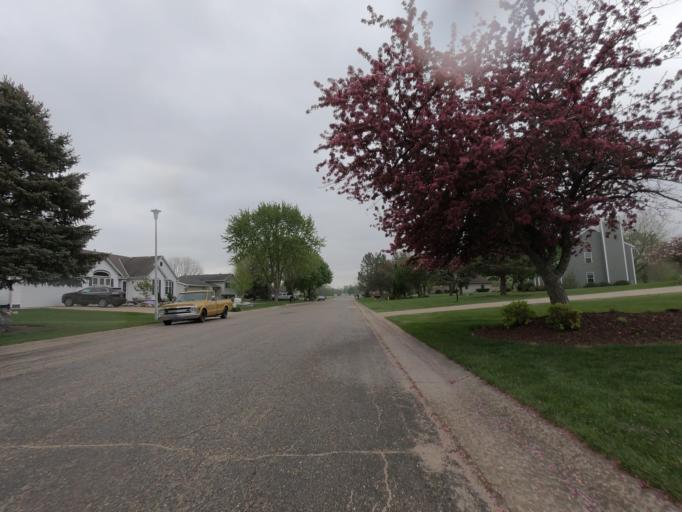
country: US
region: Wisconsin
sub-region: Jefferson County
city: Jefferson
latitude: 43.0146
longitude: -88.8114
